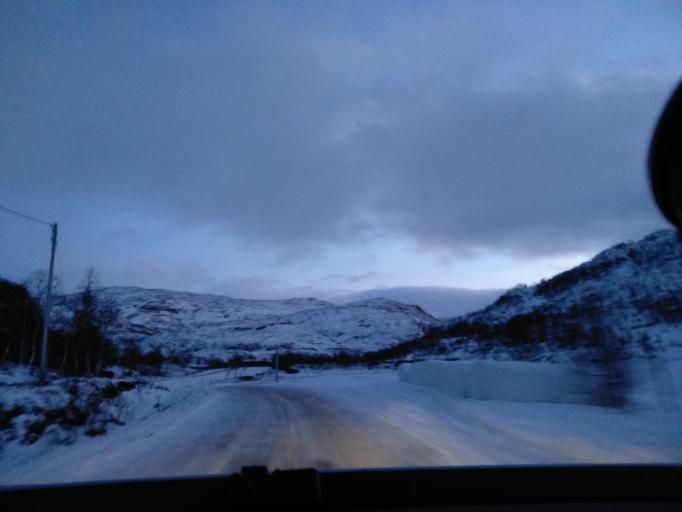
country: NO
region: Vest-Agder
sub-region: Sirdal
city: Tonstad
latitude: 59.0204
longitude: 6.9277
